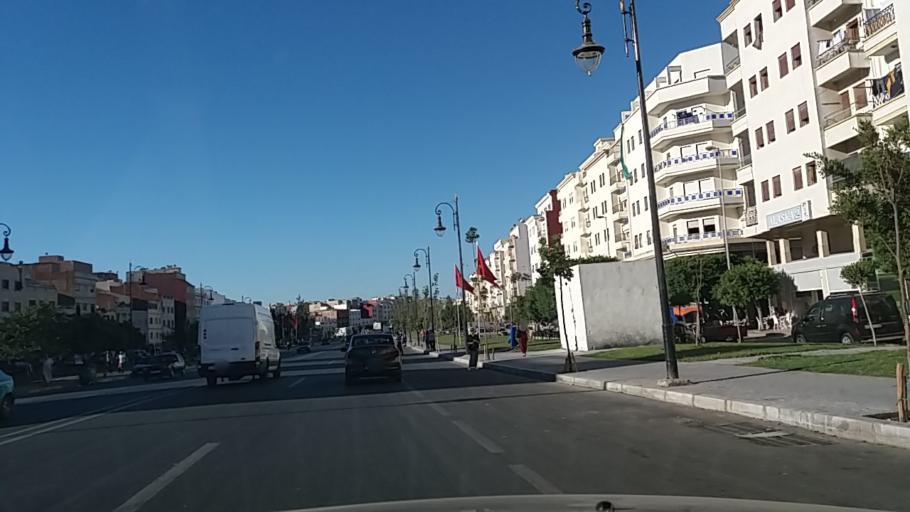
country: MA
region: Tanger-Tetouan
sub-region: Tanger-Assilah
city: Tangier
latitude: 35.7373
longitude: -5.8014
